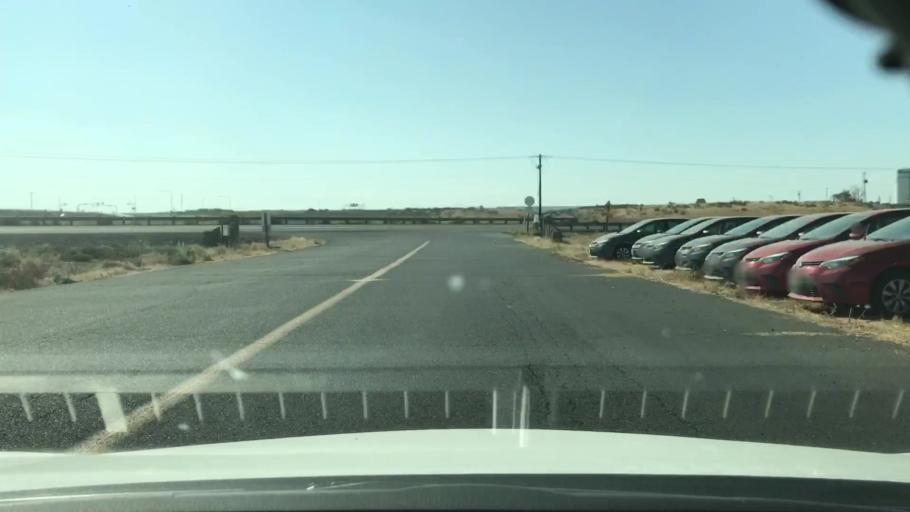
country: US
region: Washington
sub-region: Grant County
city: Moses Lake
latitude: 47.0996
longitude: -119.2349
